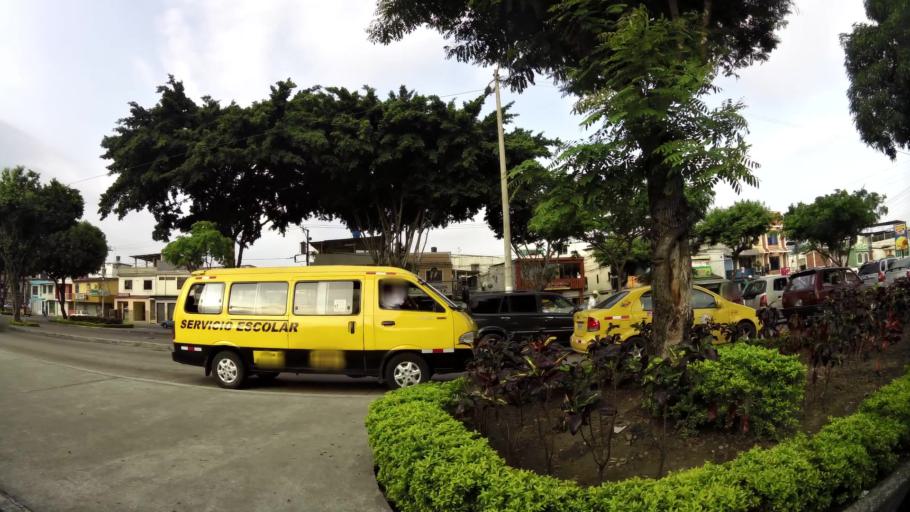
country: EC
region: Guayas
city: Eloy Alfaro
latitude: -2.1265
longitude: -79.9004
